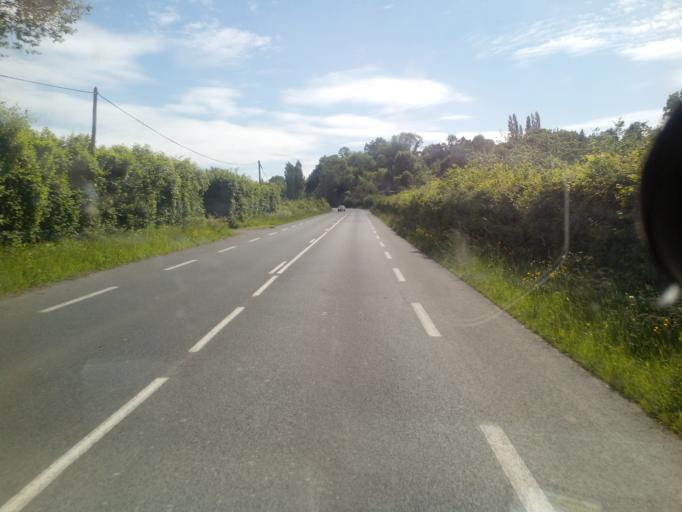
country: FR
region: Lower Normandy
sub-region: Departement du Calvados
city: Saint-Gatien-des-Bois
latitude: 49.2734
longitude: 0.1689
